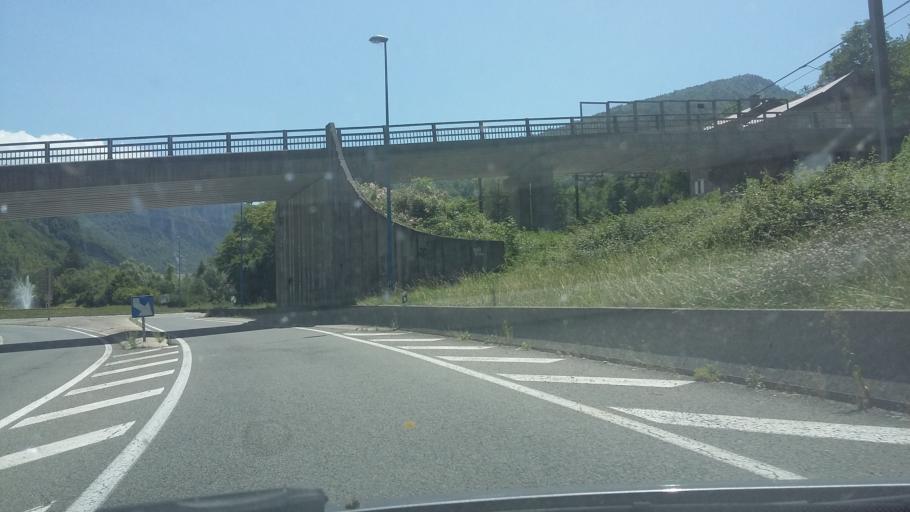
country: FR
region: Rhone-Alpes
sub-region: Departement de l'Ain
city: Tenay
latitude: 45.9324
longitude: 5.4887
